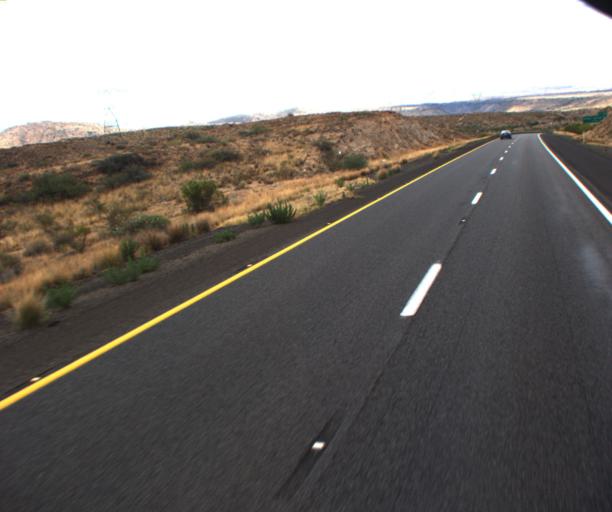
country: US
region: Arizona
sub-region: Yavapai County
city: Cordes Lakes
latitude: 34.2569
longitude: -112.1156
